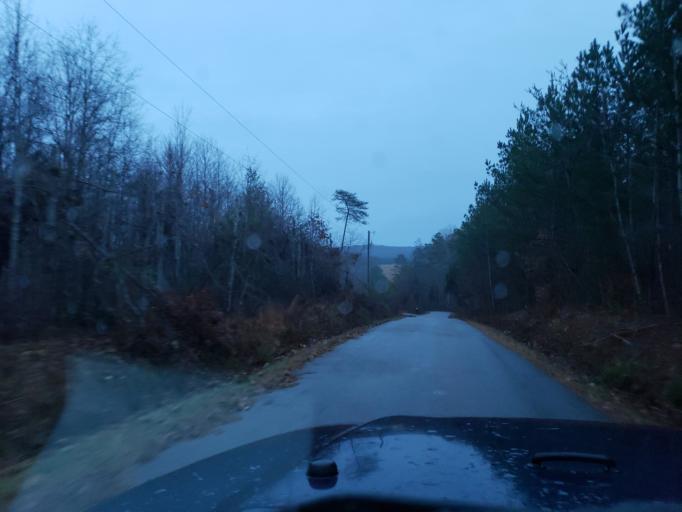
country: US
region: North Carolina
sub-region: Cleveland County
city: White Plains
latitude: 35.1480
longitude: -81.4208
